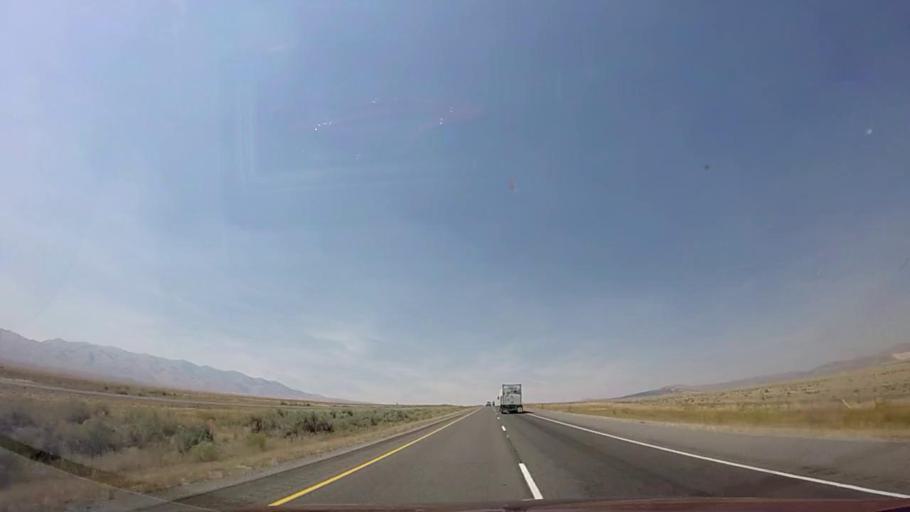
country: US
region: Idaho
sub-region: Power County
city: American Falls
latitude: 42.1201
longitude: -112.9578
